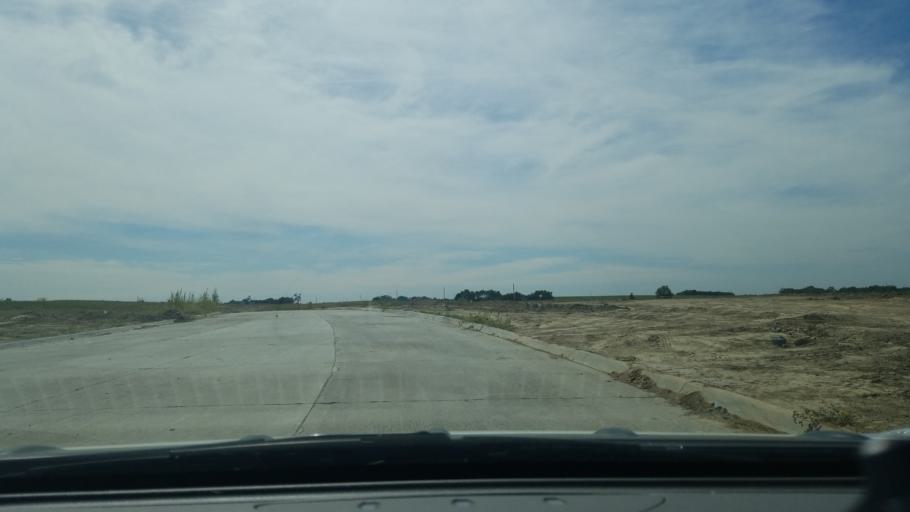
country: US
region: Nebraska
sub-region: Sarpy County
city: Chalco
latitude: 41.1454
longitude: -96.1100
